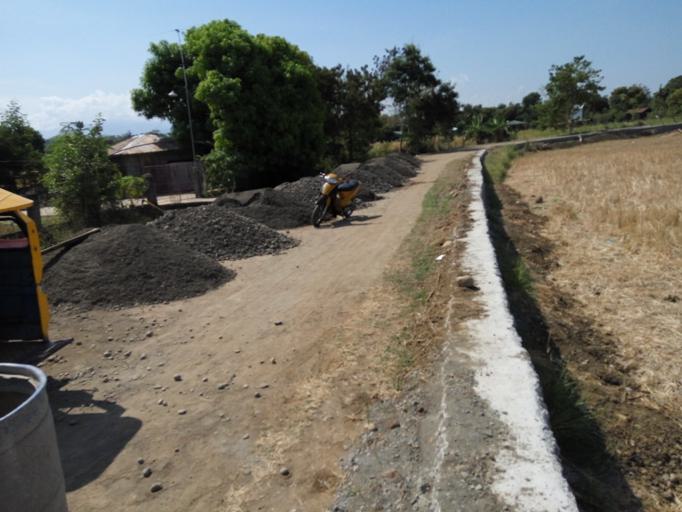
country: PH
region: Ilocos
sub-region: Province of Ilocos Sur
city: Santa Maria
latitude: 16.9458
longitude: 120.4606
